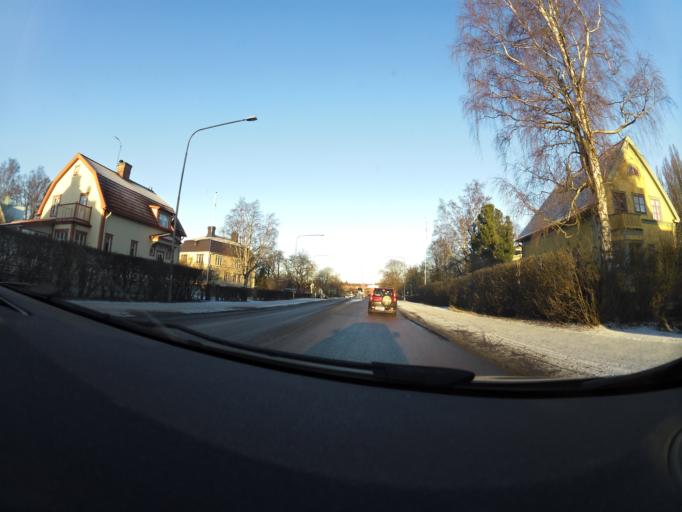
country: SE
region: Gaevleborg
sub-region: Gavle Kommun
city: Gavle
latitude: 60.6706
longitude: 17.1344
